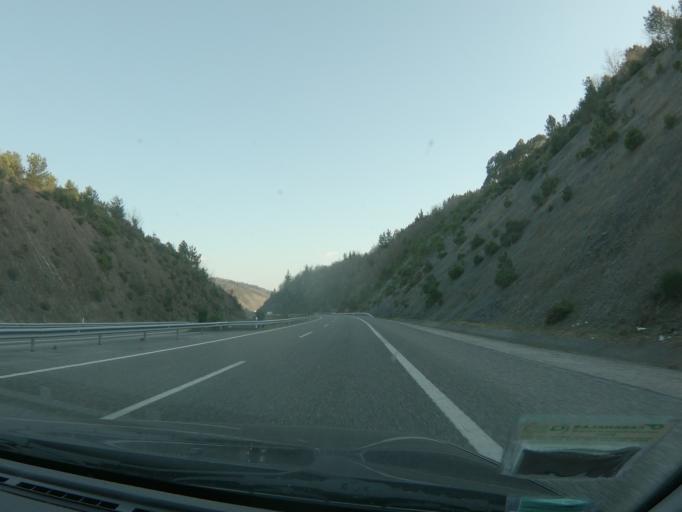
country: ES
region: Galicia
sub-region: Provincia de Lugo
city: Becerrea
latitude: 42.8541
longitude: -7.1269
